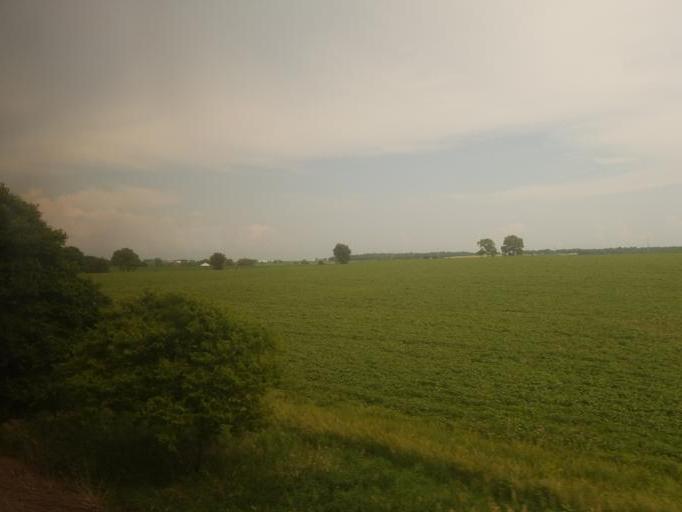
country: US
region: Illinois
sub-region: Henry County
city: Kewanee
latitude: 41.3029
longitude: -89.7297
